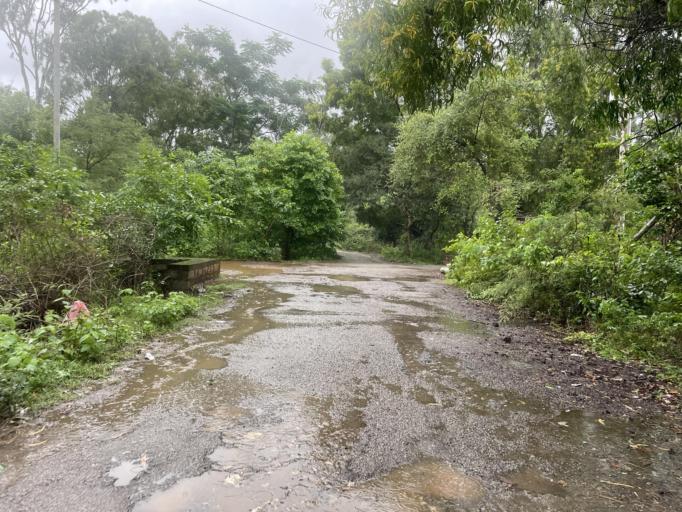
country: IN
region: Karnataka
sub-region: Bangalore Urban
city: Bangalore
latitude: 12.9423
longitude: 77.5026
